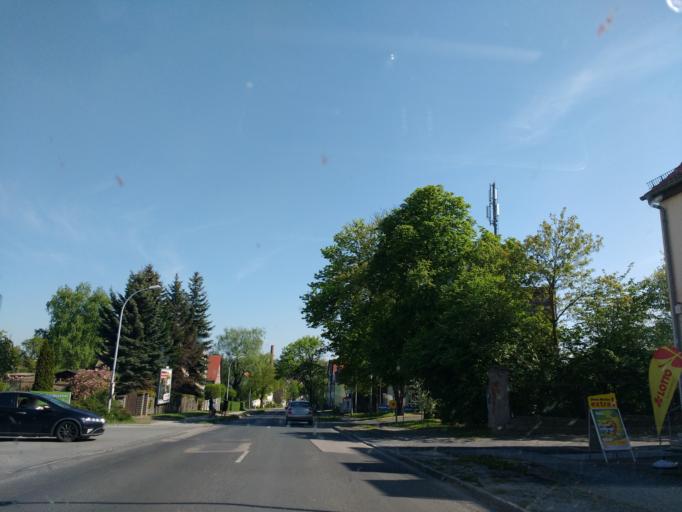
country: DE
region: Saxony-Anhalt
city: Zeitz
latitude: 51.0637
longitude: 12.1268
